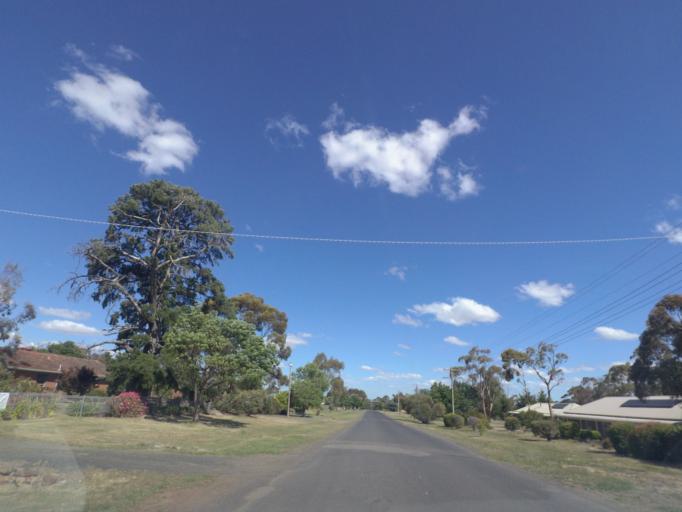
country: AU
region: Victoria
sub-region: Hume
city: Sunbury
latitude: -37.4612
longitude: 144.6696
